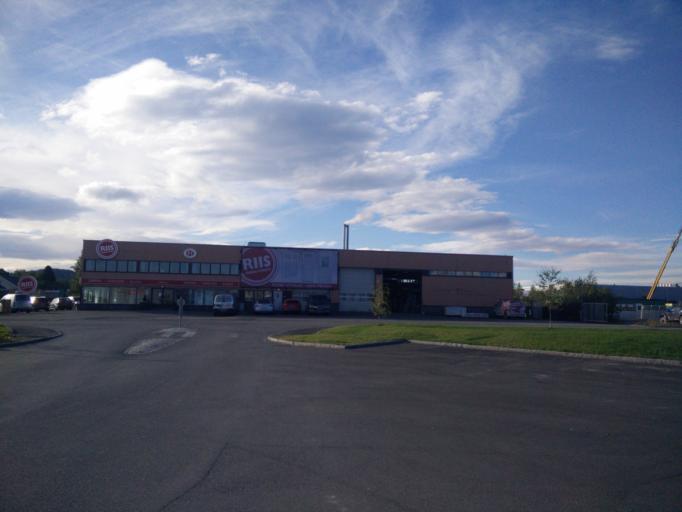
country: NO
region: Sor-Trondelag
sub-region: Trondheim
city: Trondheim
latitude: 63.3531
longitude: 10.3747
